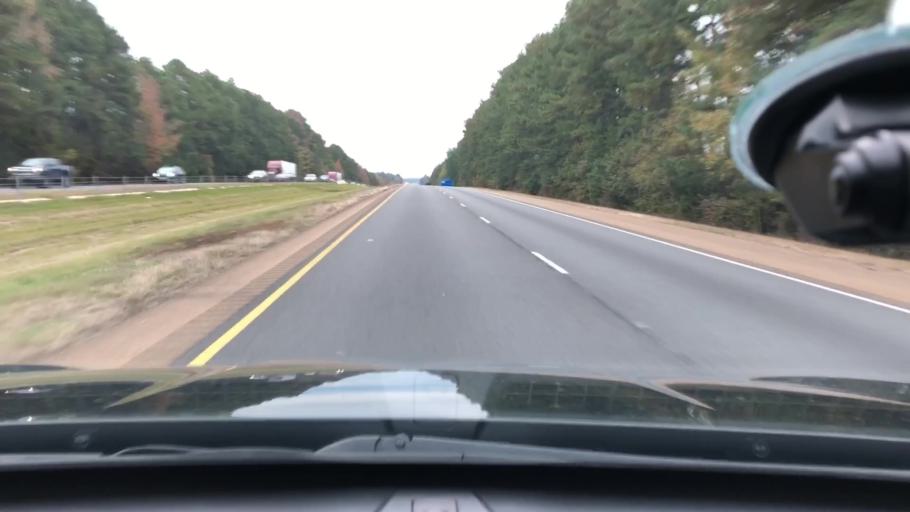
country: US
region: Arkansas
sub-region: Clark County
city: Gurdon
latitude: 33.9752
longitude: -93.2052
